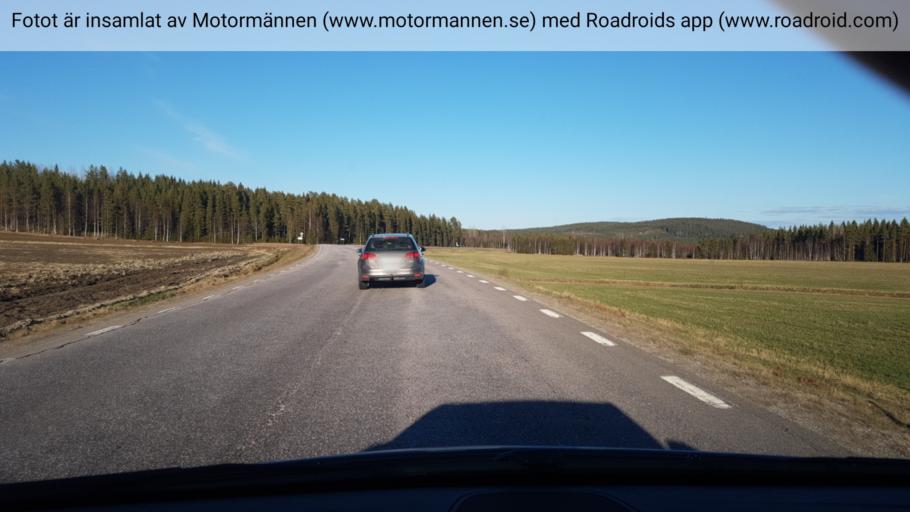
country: SE
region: Vaesterbotten
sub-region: Vindelns Kommun
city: Vindeln
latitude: 64.0537
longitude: 19.6602
